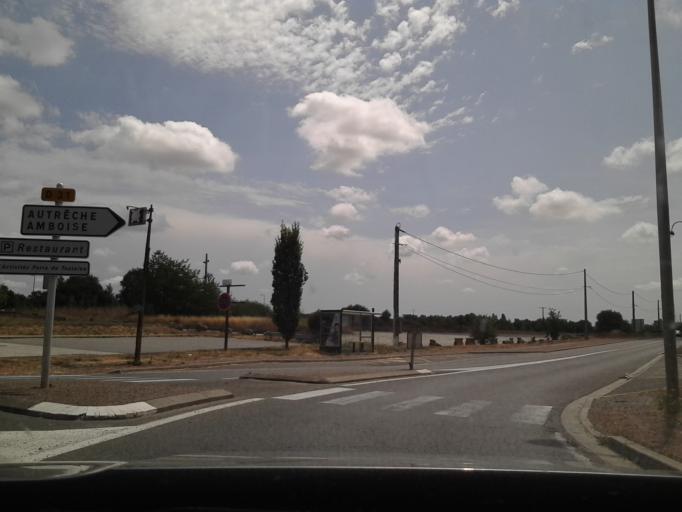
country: FR
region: Centre
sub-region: Departement d'Indre-et-Loire
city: Auzouer-en-Touraine
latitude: 47.5373
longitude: 0.9858
